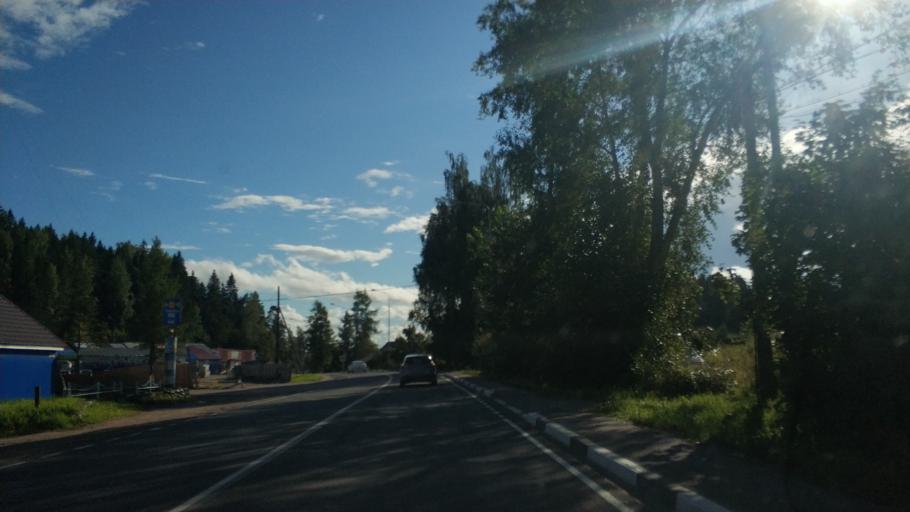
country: RU
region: Republic of Karelia
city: Lakhdenpokh'ya
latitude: 61.5268
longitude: 30.2024
